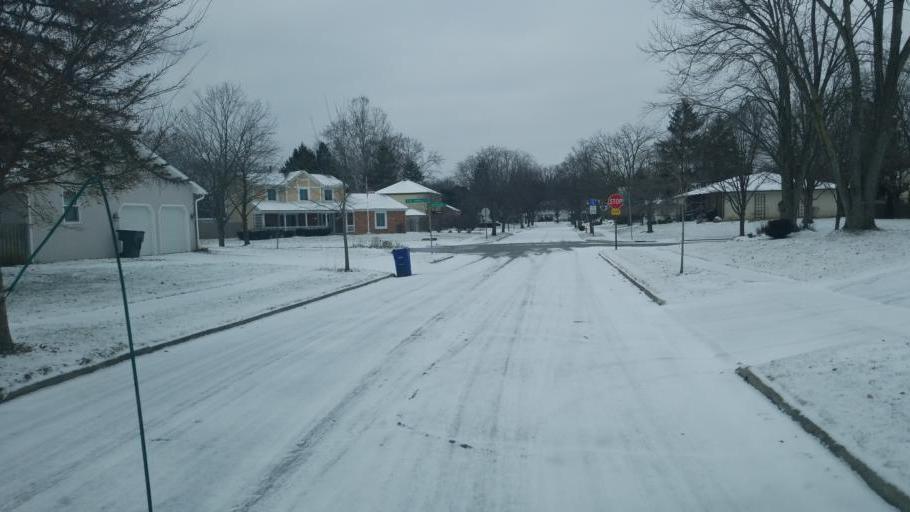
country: US
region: Ohio
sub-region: Delaware County
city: Powell
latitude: 40.1235
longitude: -83.0814
